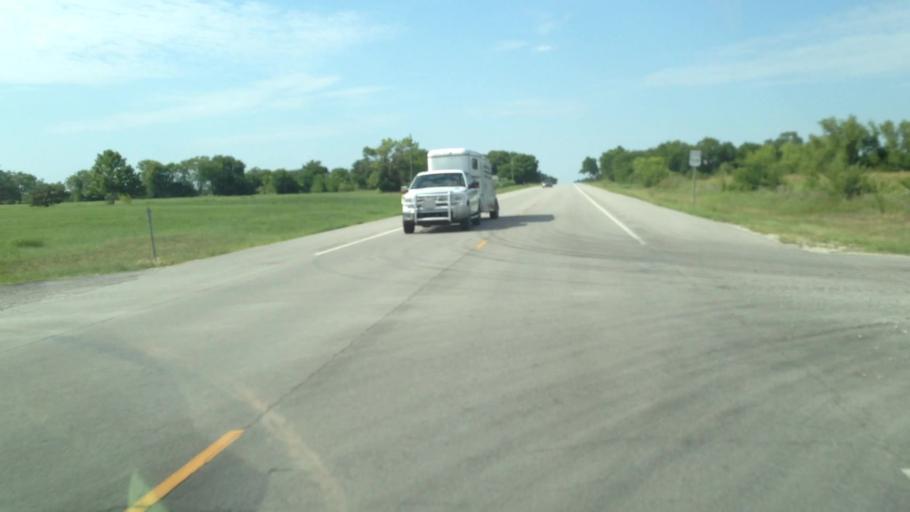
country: US
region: Kansas
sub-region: Labette County
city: Altamont
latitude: 37.2518
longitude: -95.2671
